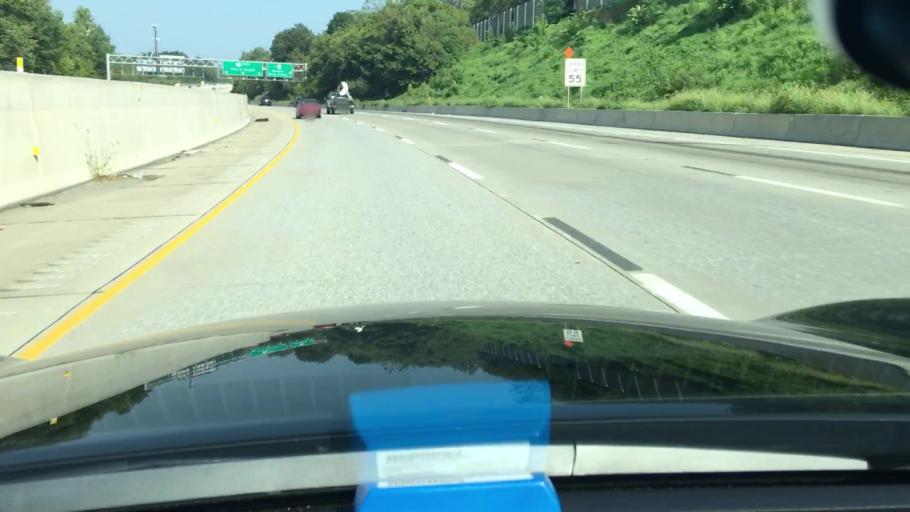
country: US
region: Pennsylvania
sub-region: Chester County
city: Malvern
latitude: 40.0509
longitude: -75.5468
